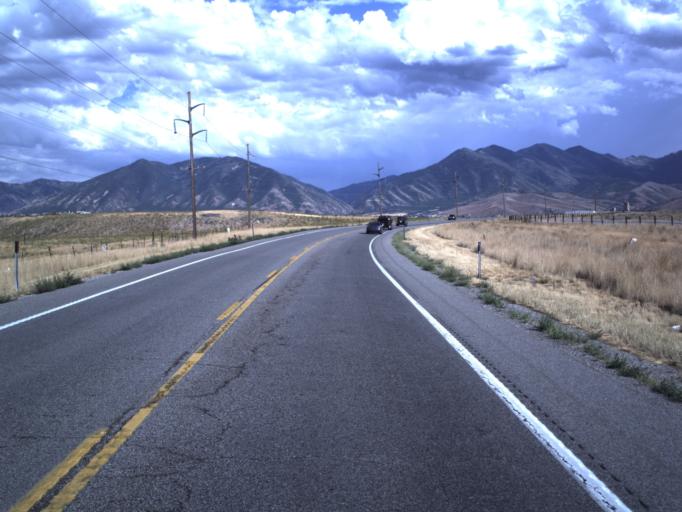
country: US
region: Utah
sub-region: Tooele County
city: Tooele
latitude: 40.5619
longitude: -112.3562
